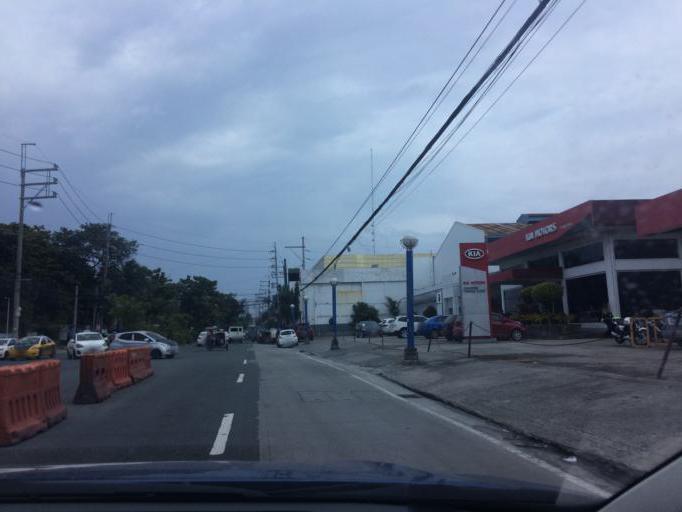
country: PH
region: Metro Manila
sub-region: Makati City
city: Makati City
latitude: 14.5296
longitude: 121.0048
